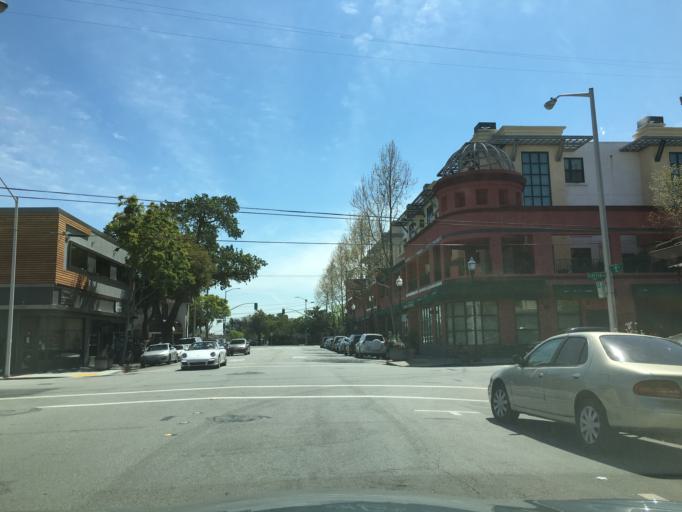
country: US
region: California
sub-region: San Mateo County
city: San Mateo
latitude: 37.5624
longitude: -122.3190
